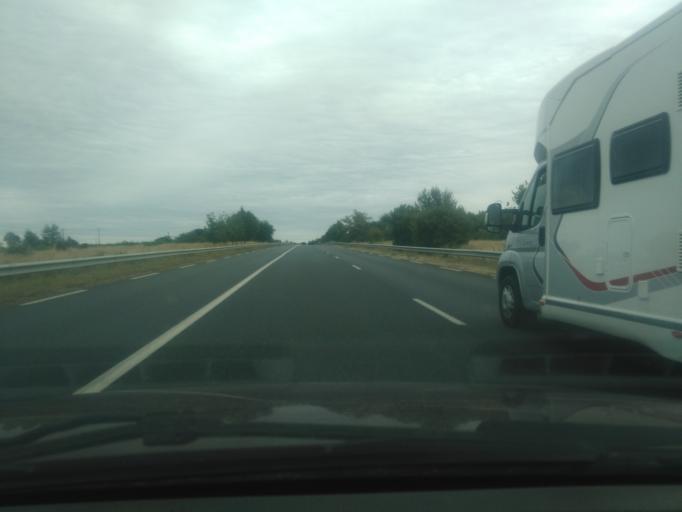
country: FR
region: Centre
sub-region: Departement de l'Indre
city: Le Pechereau
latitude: 46.5971
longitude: 1.5436
